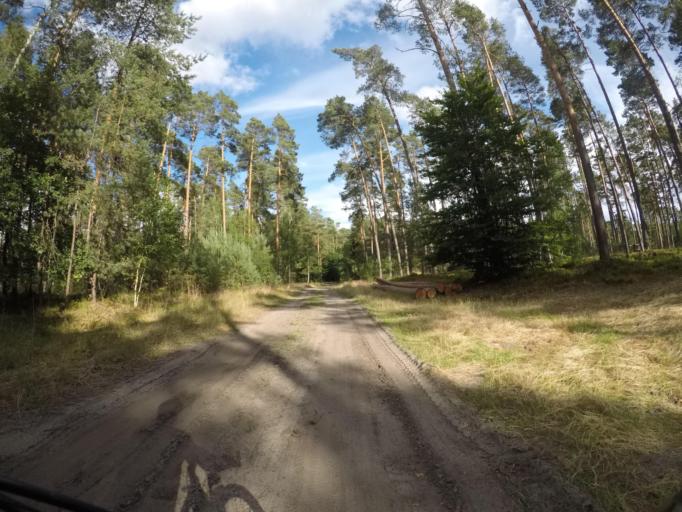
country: DE
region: Lower Saxony
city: Neu Darchau
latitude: 53.2711
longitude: 10.9775
